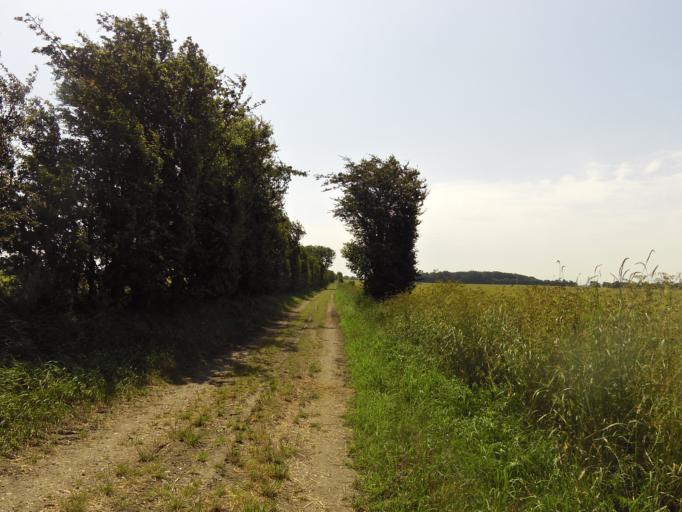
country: DK
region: South Denmark
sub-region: Aabenraa Kommune
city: Rodekro
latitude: 55.1523
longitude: 9.2480
